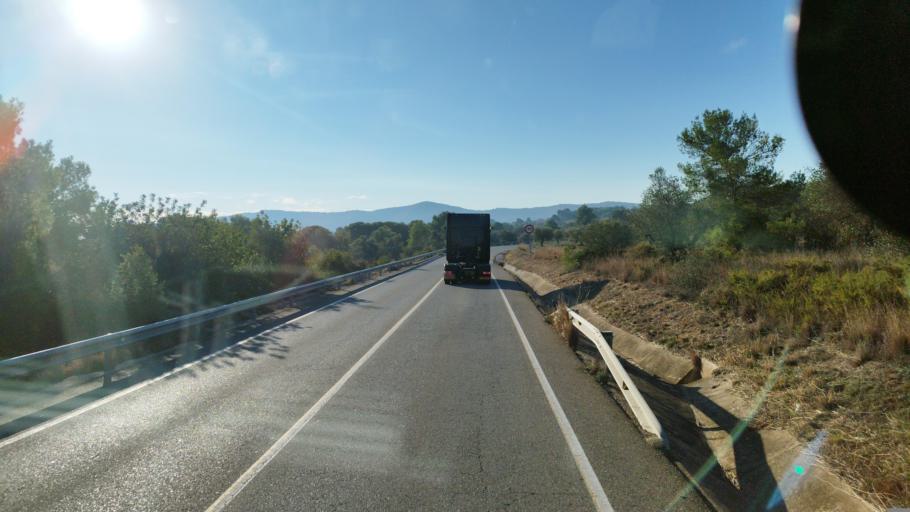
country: ES
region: Catalonia
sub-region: Provincia de Tarragona
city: Albinyana
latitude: 41.2635
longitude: 1.4974
